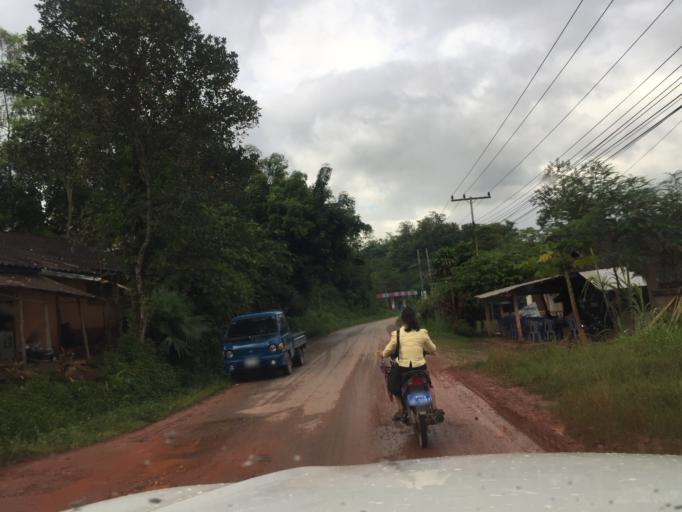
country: LA
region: Oudomxai
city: Muang La
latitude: 20.8588
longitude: 102.1137
